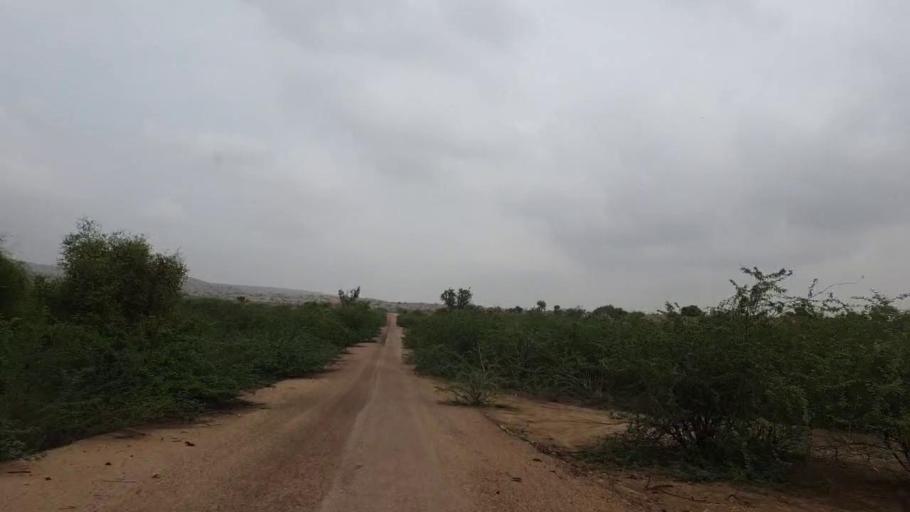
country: PK
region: Sindh
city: Diplo
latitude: 24.5188
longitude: 69.4707
